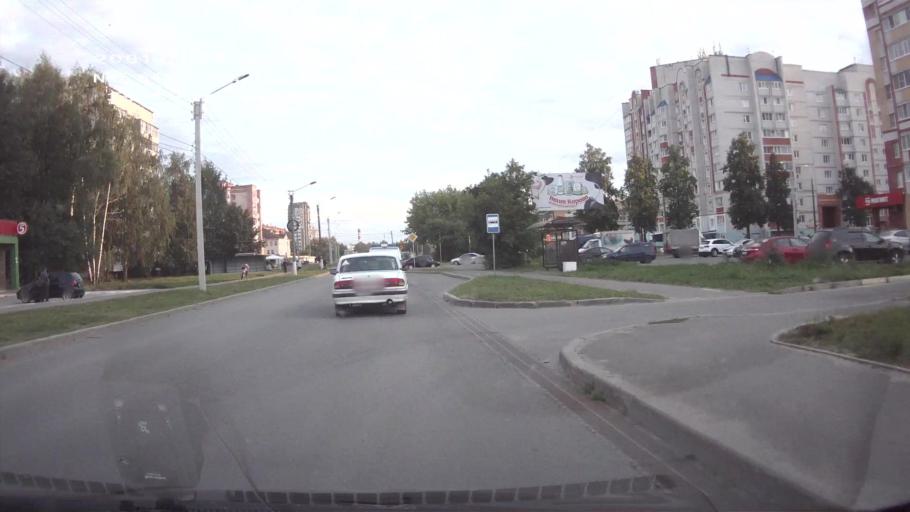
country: RU
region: Mariy-El
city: Yoshkar-Ola
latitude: 56.6461
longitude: 47.8566
